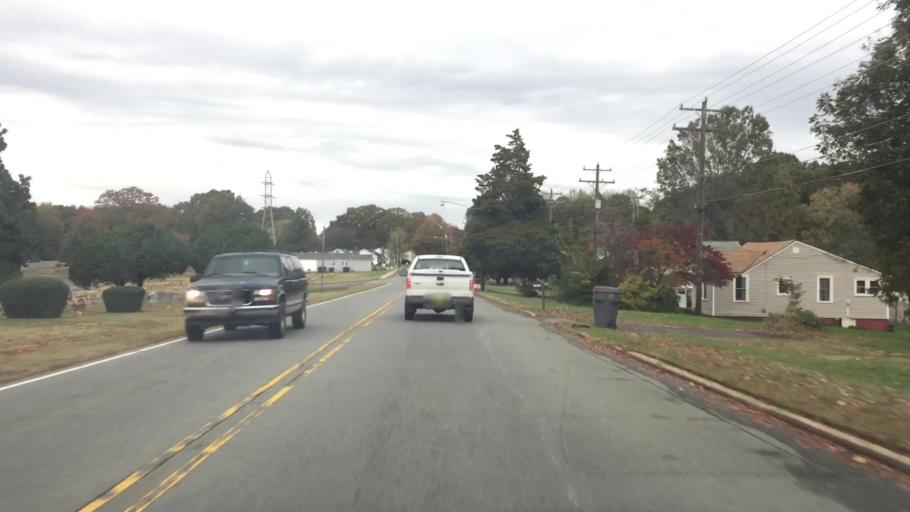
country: US
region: North Carolina
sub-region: Rockingham County
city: Reidsville
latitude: 36.3411
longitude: -79.6535
